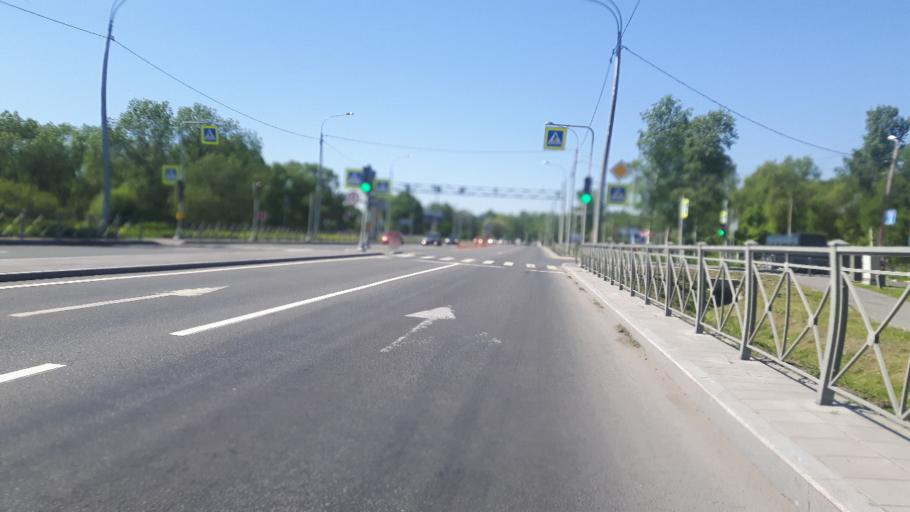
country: RU
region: Leningrad
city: Gorbunki
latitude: 59.8688
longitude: 29.9748
